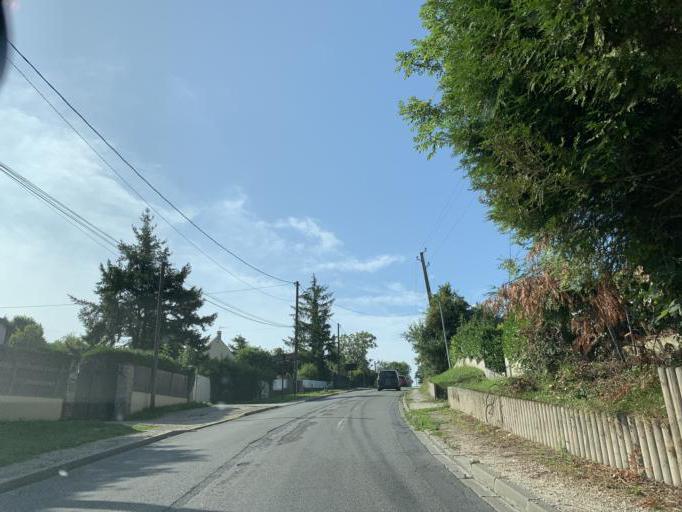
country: FR
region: Ile-de-France
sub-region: Departement de Seine-et-Marne
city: Chalifert
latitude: 48.8969
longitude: 2.7746
